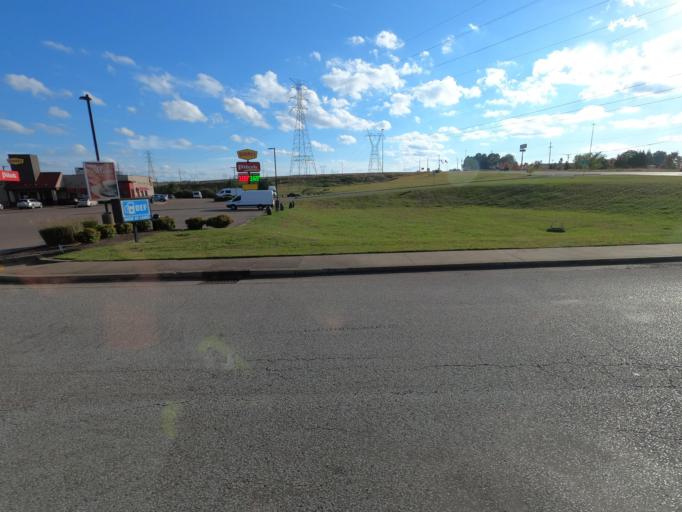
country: US
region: Tennessee
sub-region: Madison County
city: Jackson
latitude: 35.6837
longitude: -88.7783
